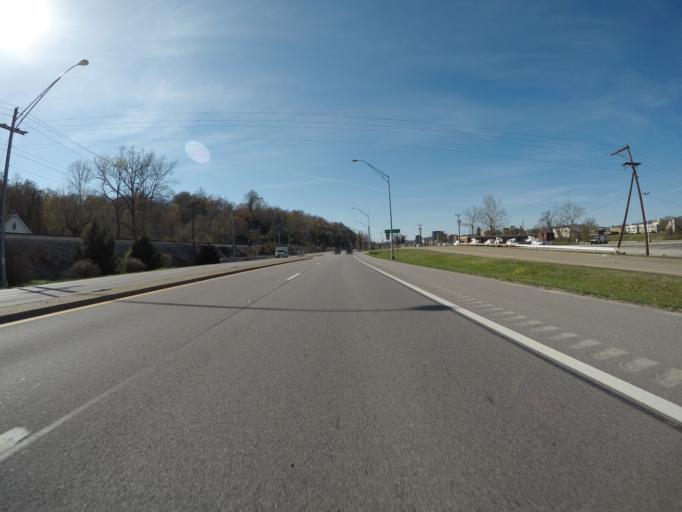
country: US
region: West Virginia
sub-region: Kanawha County
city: Charleston
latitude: 38.3376
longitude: -81.6281
